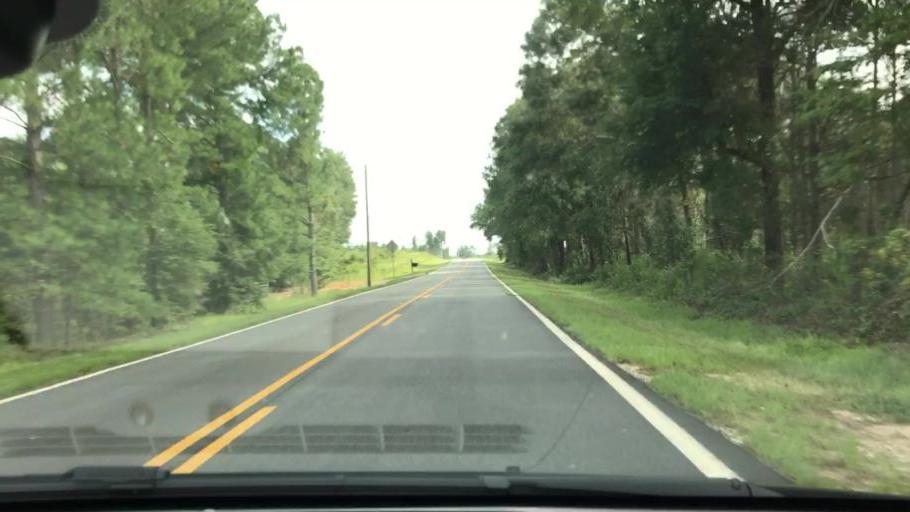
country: US
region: Georgia
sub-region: Clay County
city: Fort Gaines
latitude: 31.5470
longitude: -84.9652
